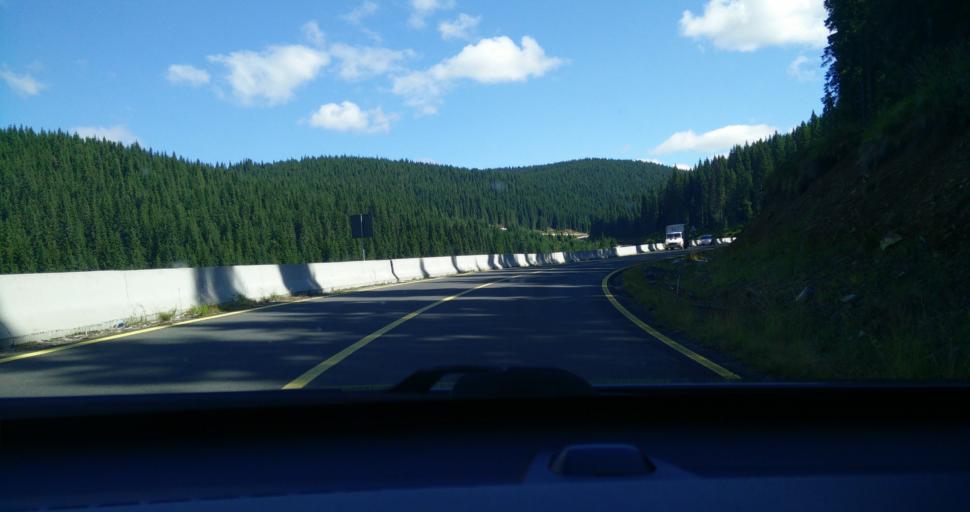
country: RO
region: Hunedoara
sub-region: Oras Petrila
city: Petrila
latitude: 45.4568
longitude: 23.6132
